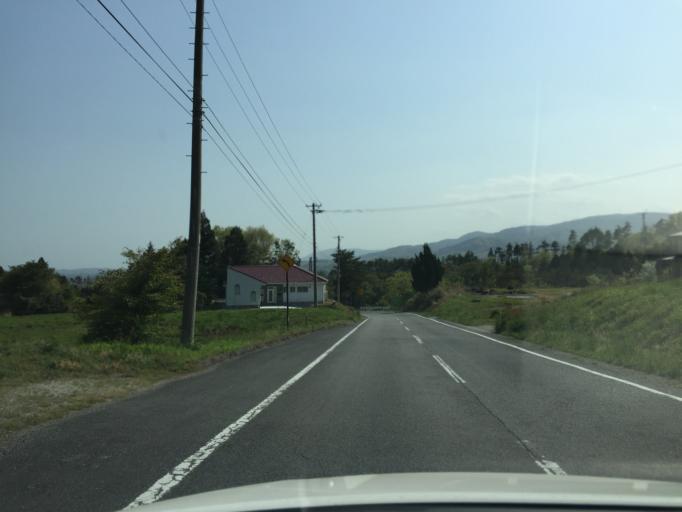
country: JP
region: Fukushima
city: Iwaki
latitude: 37.1559
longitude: 140.8605
